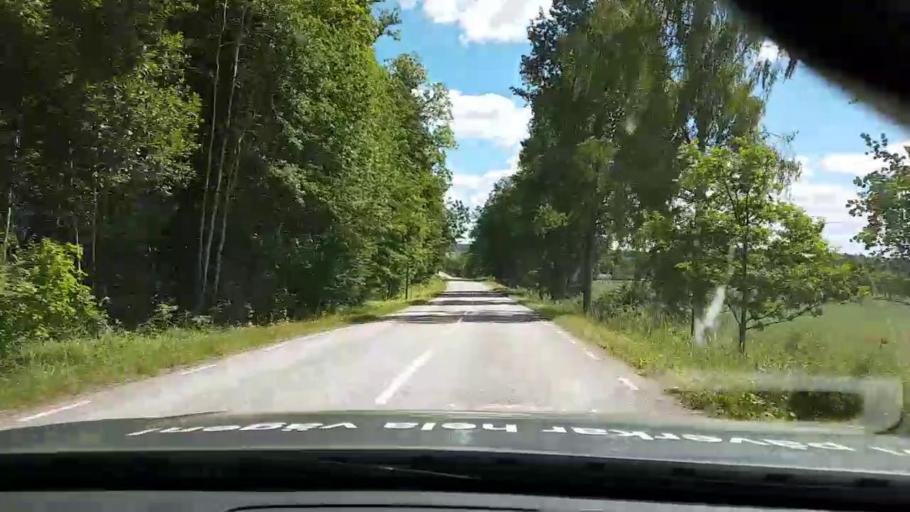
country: SE
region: Kalmar
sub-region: Vasterviks Kommun
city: Overum
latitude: 58.0774
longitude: 16.3581
